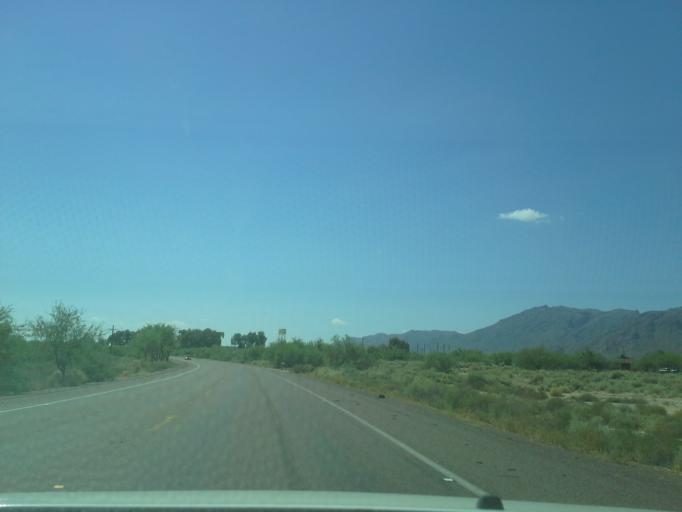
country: US
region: Arizona
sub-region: Maricopa County
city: Laveen
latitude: 33.2811
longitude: -112.1689
